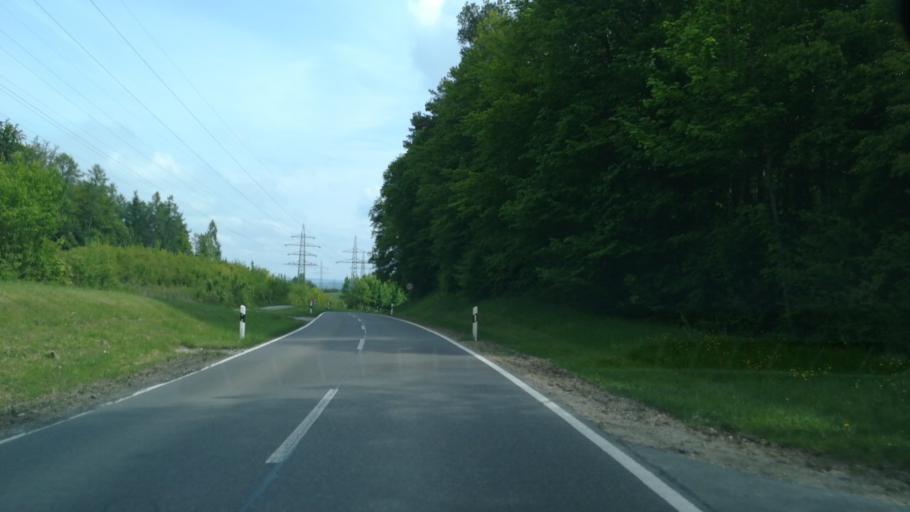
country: DE
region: Baden-Wuerttemberg
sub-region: Freiburg Region
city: Singen
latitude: 47.7750
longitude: 8.8632
